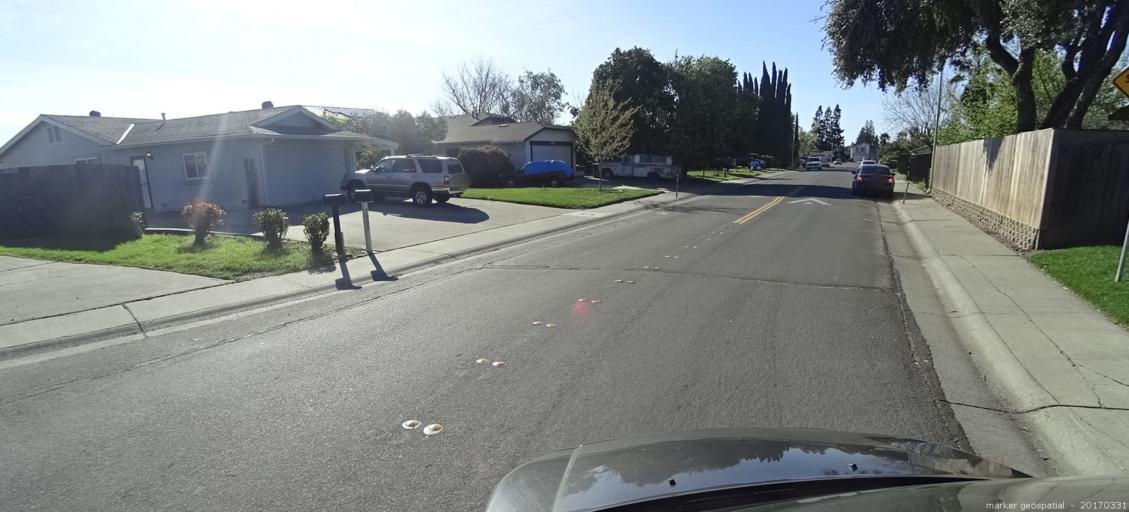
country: US
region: California
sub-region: Sacramento County
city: Parkway
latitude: 38.4723
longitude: -121.4522
